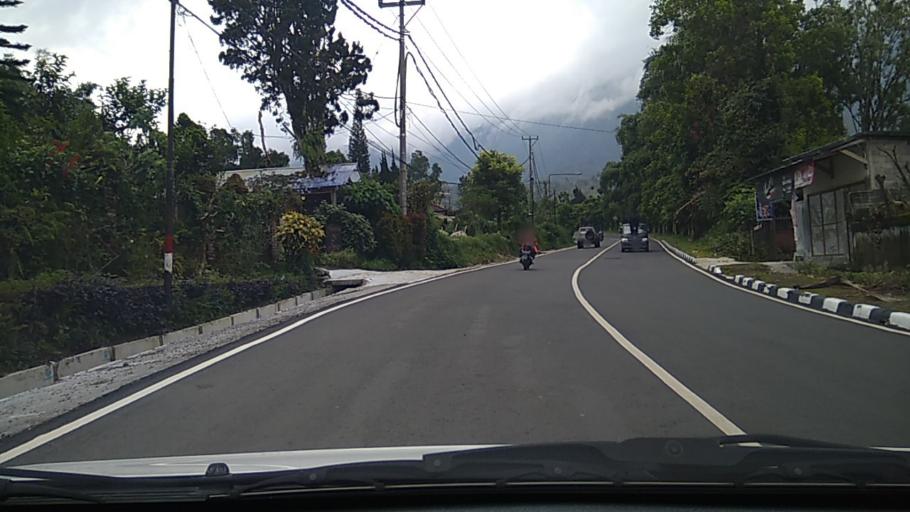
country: ID
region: Bali
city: Munduk
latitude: -8.2653
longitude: 115.1646
